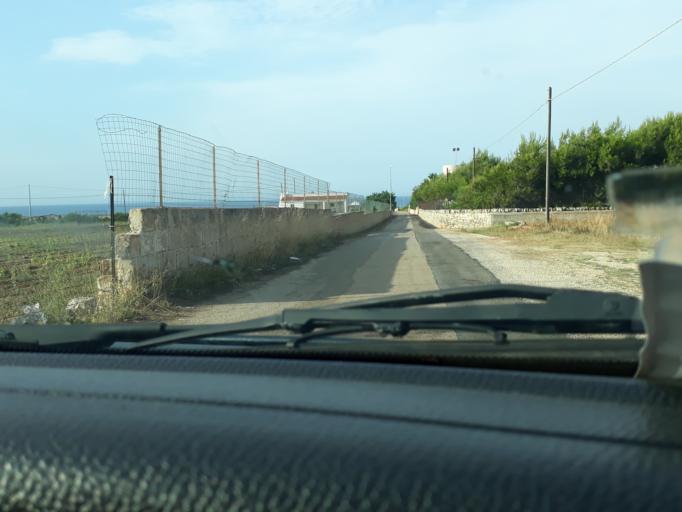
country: IT
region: Apulia
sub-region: Provincia di Brindisi
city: Carovigno
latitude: 40.7612
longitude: 17.6844
